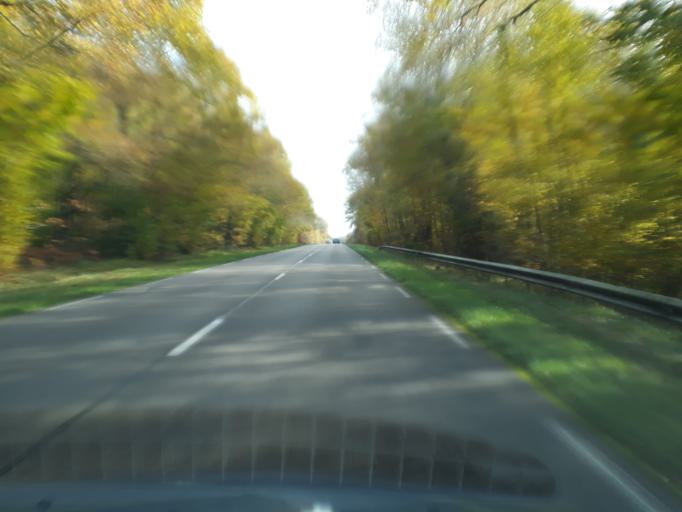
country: FR
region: Ile-de-France
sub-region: Departement de Seine-et-Marne
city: Champagne-sur-Seine
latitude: 48.4197
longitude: 2.8183
